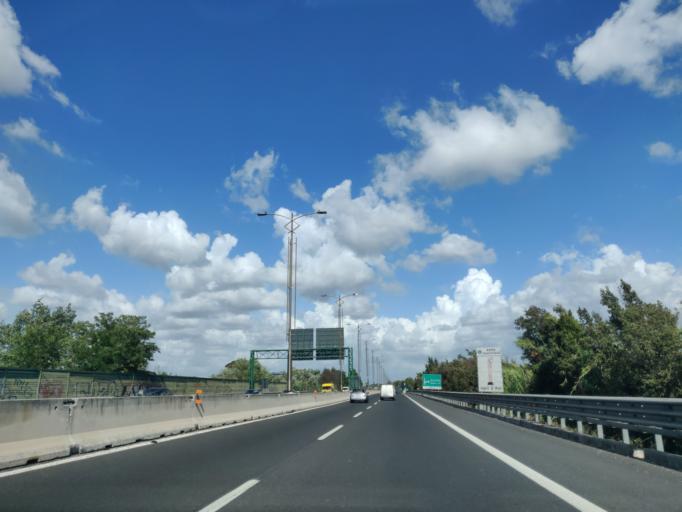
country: IT
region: Latium
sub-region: Citta metropolitana di Roma Capitale
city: Vitinia
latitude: 41.8190
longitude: 12.3990
